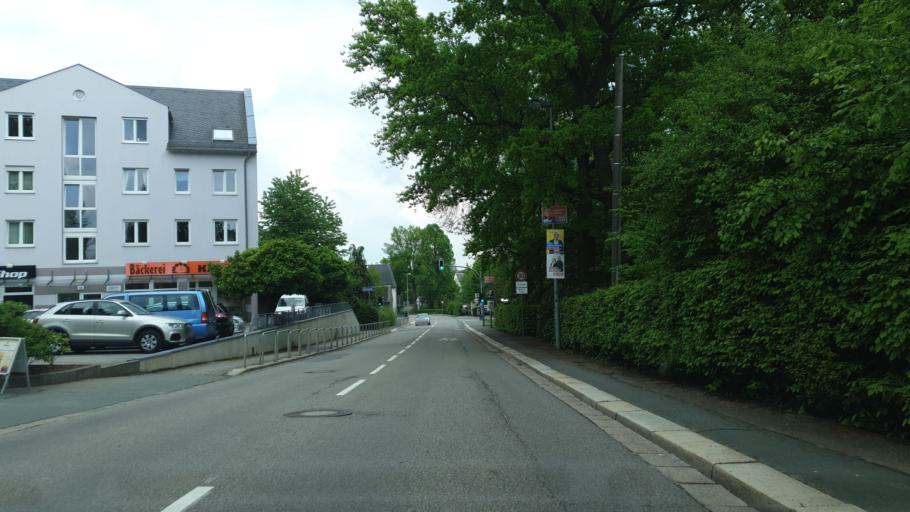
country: DE
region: Saxony
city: Wittgensdorf
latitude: 50.8618
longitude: 12.8339
